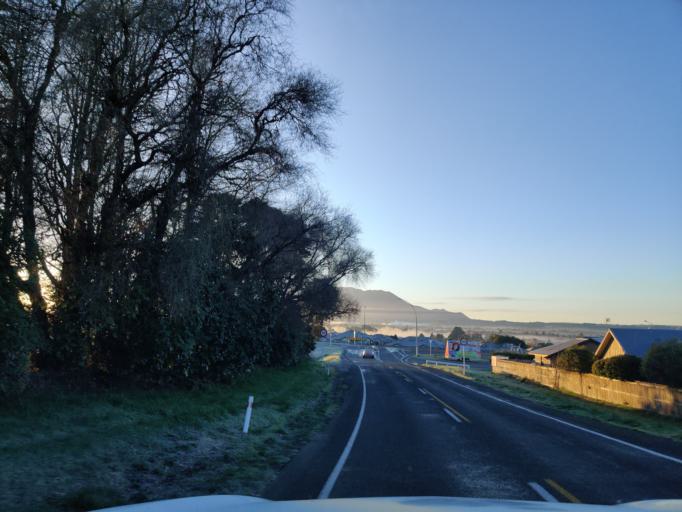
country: NZ
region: Waikato
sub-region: Taupo District
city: Taupo
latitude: -38.6730
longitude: 176.0679
